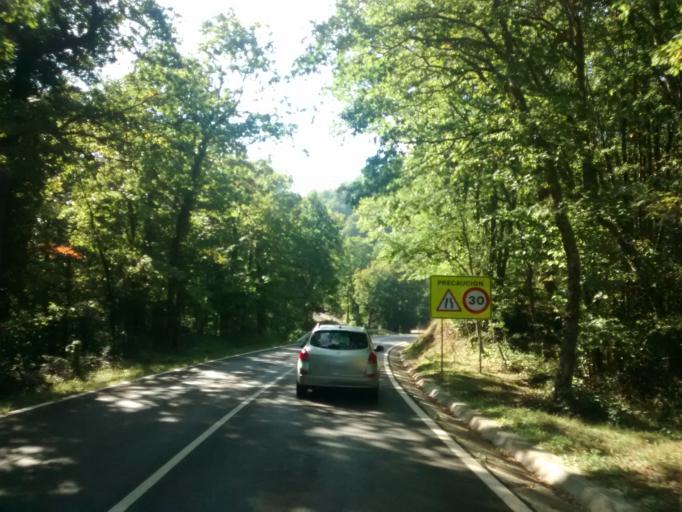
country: ES
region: Cantabria
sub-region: Provincia de Cantabria
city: Reinosa
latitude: 42.9611
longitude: -4.0593
